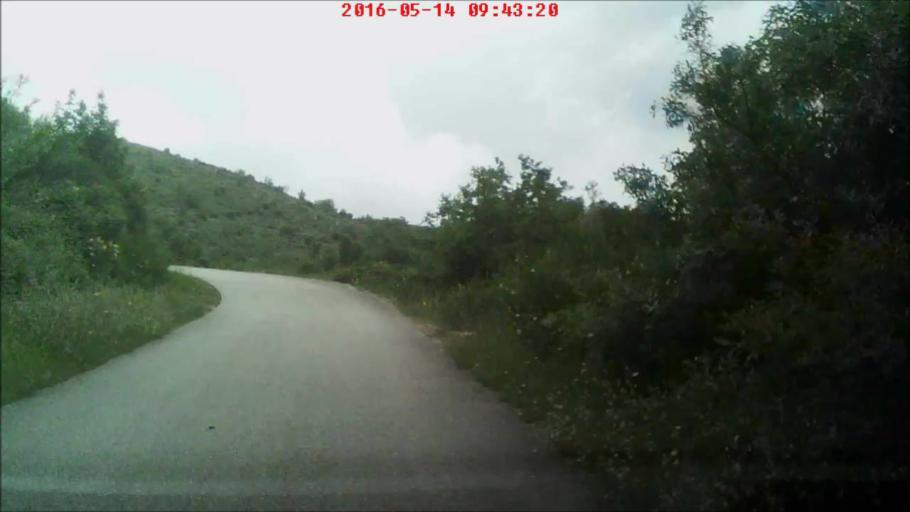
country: HR
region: Dubrovacko-Neretvanska
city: Podgora
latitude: 42.7863
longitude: 17.9046
